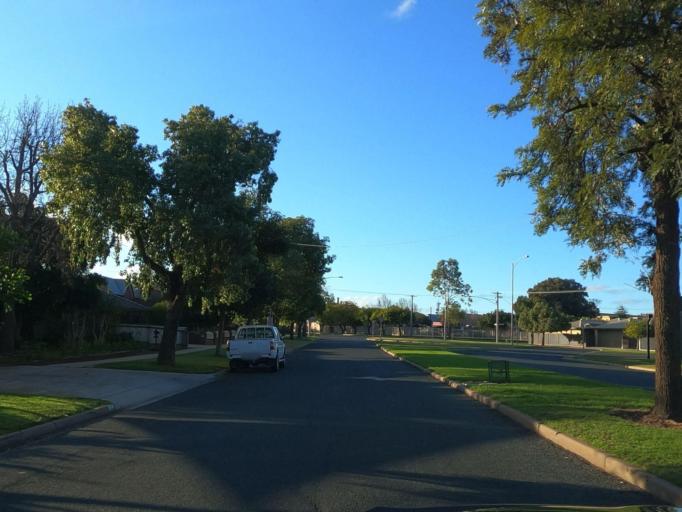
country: AU
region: Victoria
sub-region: Swan Hill
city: Swan Hill
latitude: -35.3446
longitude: 143.5561
